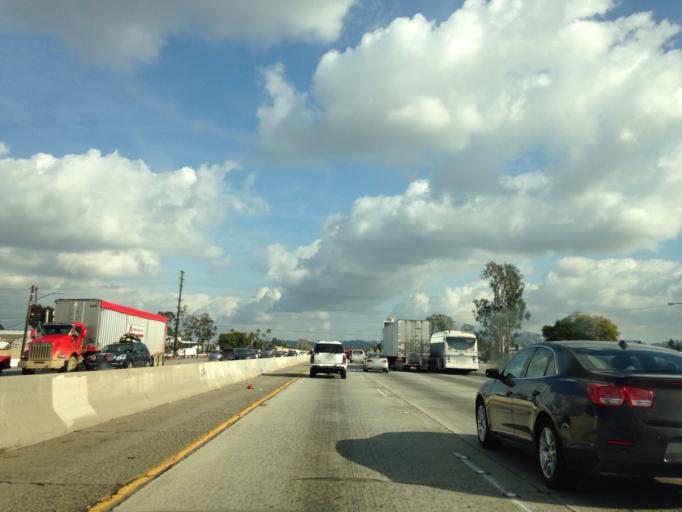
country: US
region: California
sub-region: Los Angeles County
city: West Covina
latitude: 34.0722
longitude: -117.9129
